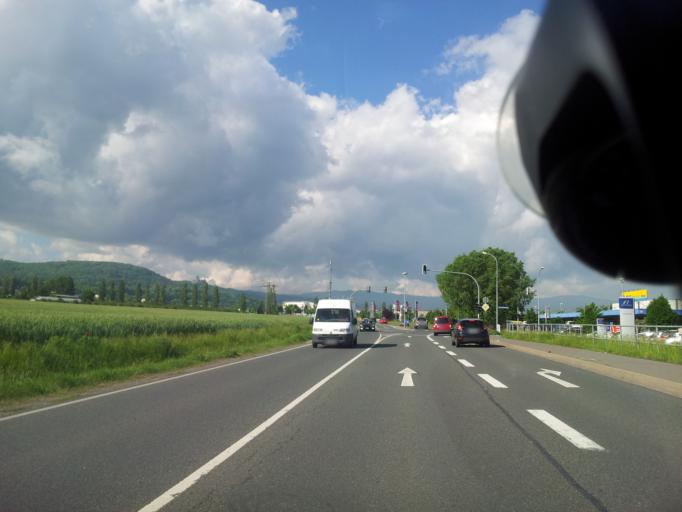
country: DE
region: Saxony-Anhalt
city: Wernigerode
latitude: 51.8484
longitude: 10.8144
